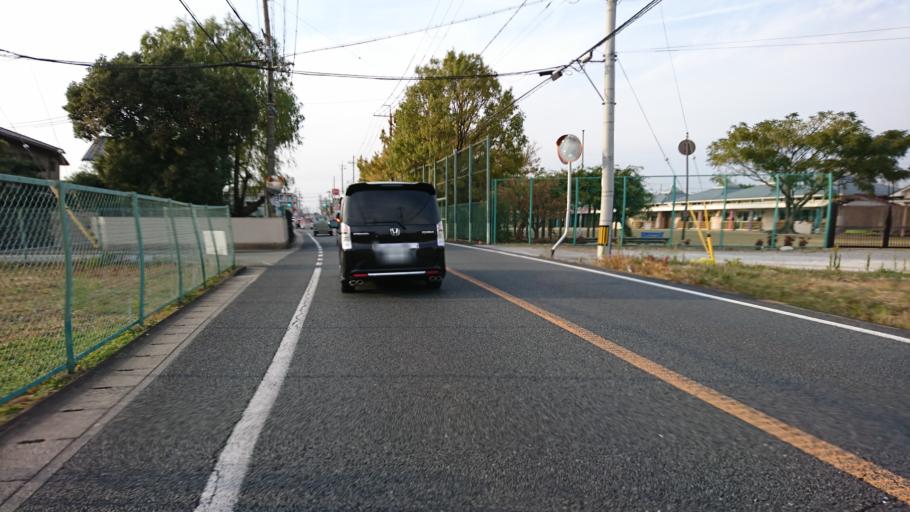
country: JP
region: Hyogo
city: Kakogawacho-honmachi
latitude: 34.7301
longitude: 134.8382
